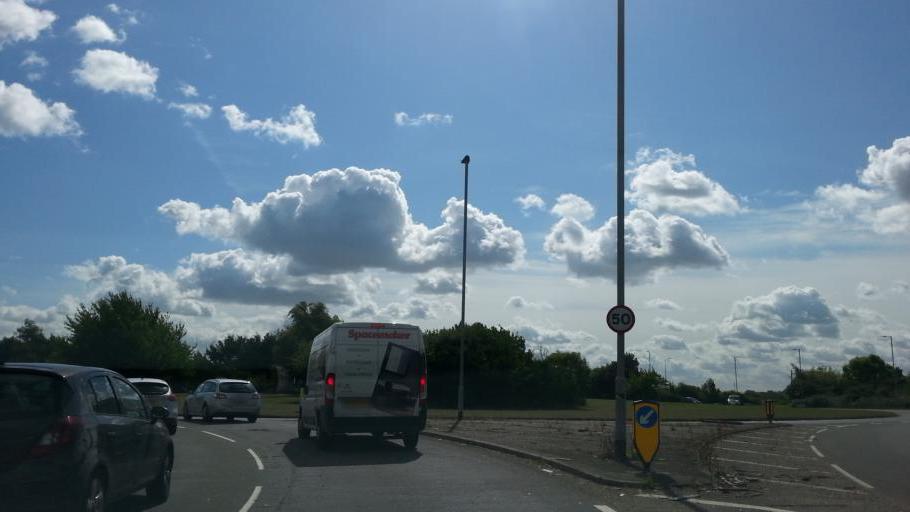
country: GB
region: England
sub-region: Essex
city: South Benfleet
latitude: 51.5367
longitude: 0.5629
